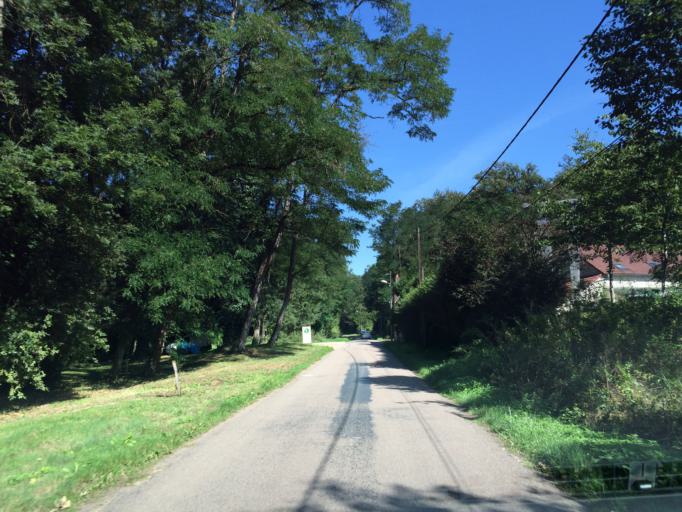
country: FR
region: Bourgogne
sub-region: Departement de l'Yonne
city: Fleury-la-Vallee
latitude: 47.8512
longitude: 3.3998
